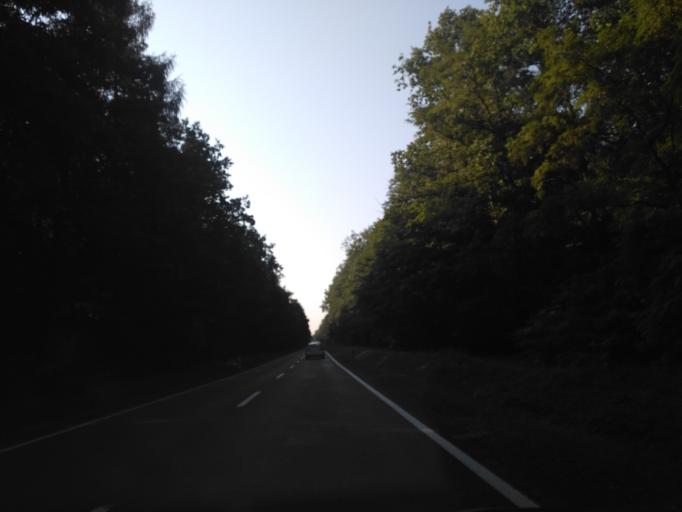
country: PL
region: Subcarpathian Voivodeship
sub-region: Powiat nizanski
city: Nisko
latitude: 50.4838
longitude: 22.1443
